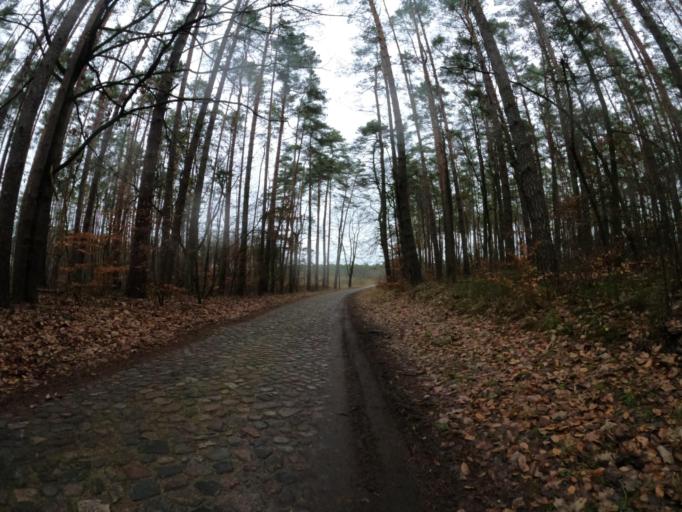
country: PL
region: West Pomeranian Voivodeship
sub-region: Powiat mysliborski
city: Debno
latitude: 52.7181
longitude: 14.7277
